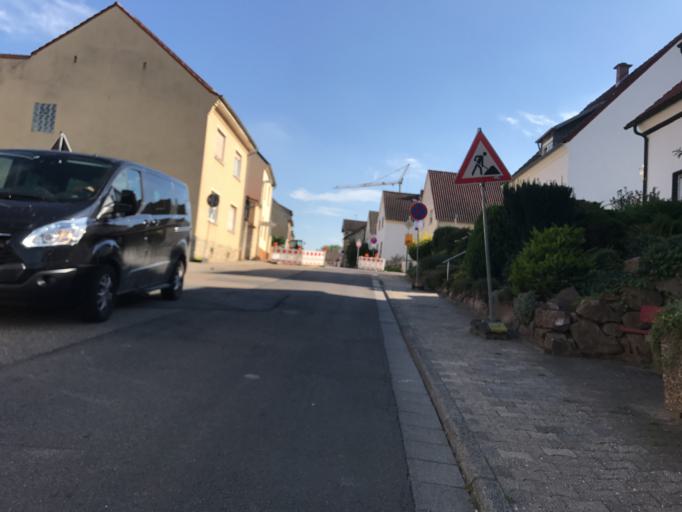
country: DE
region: Rheinland-Pfalz
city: Wackernheim
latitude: 49.9761
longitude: 8.1185
